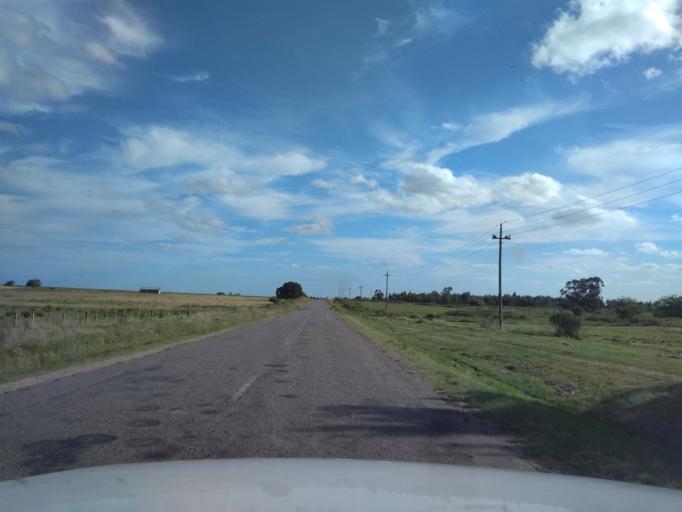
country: UY
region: Canelones
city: San Ramon
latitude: -34.2554
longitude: -55.9266
